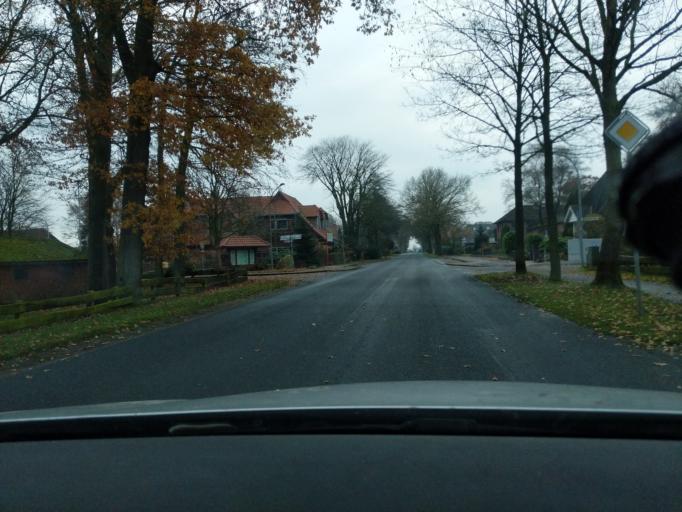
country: DE
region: Lower Saxony
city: Ahlerstedt
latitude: 53.3966
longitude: 9.4884
